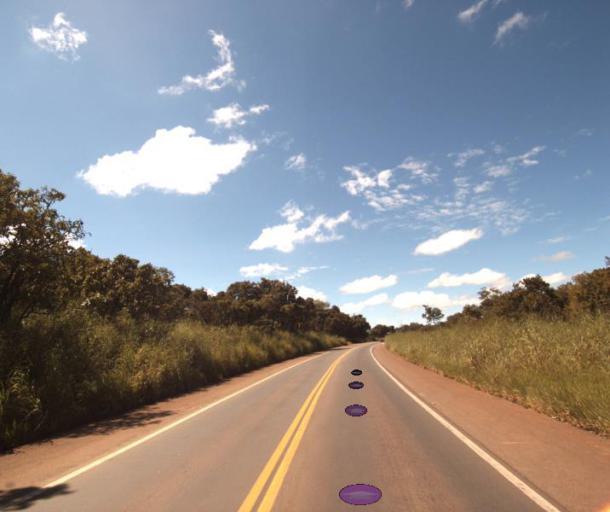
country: BR
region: Goias
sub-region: Rialma
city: Rialma
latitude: -15.3991
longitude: -49.5378
